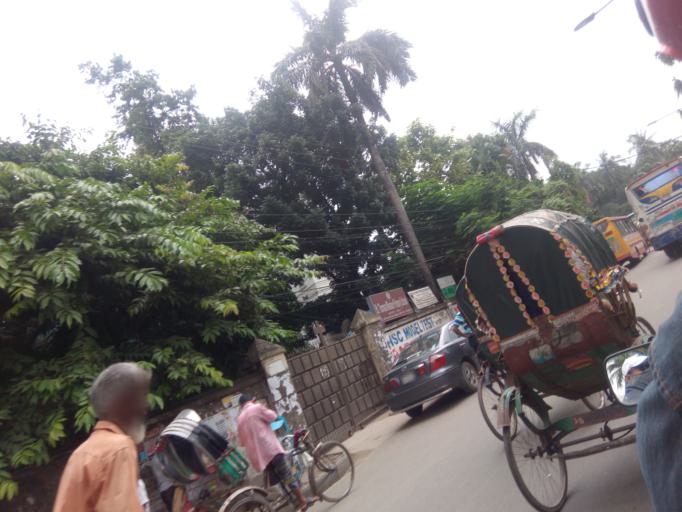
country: BD
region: Dhaka
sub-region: Dhaka
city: Dhaka
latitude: 23.7105
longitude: 90.4118
